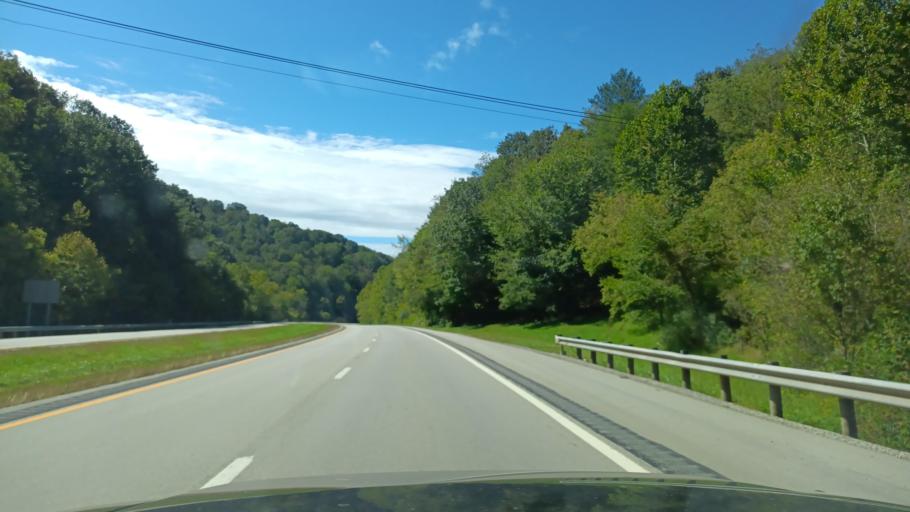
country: US
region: West Virginia
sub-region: Harrison County
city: Salem
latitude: 39.2850
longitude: -80.6582
